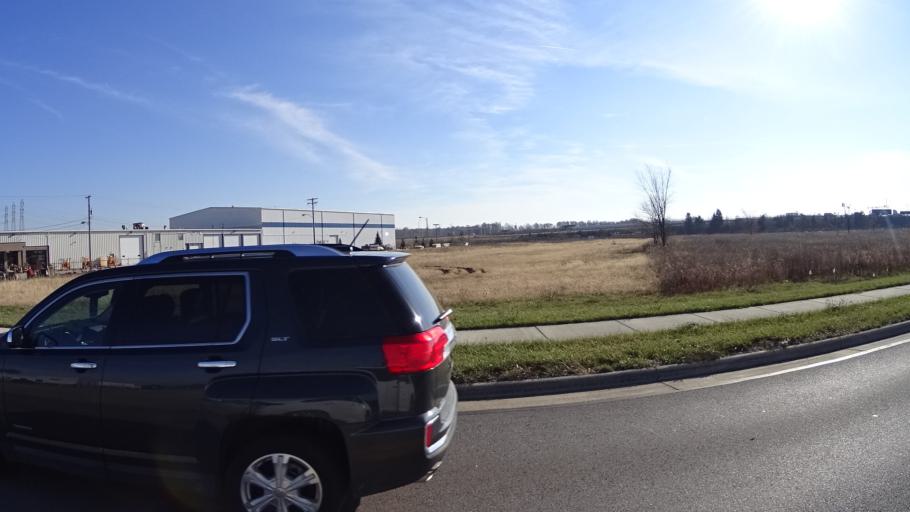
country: US
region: Ohio
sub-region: Lorain County
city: Avon
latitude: 41.4668
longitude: -82.0547
